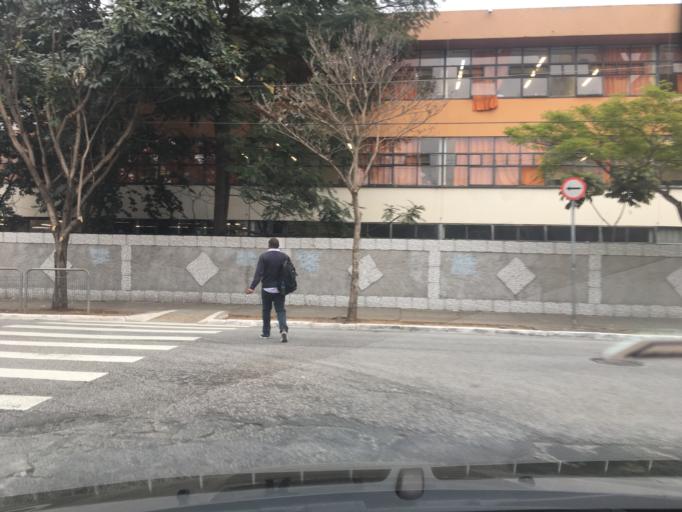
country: BR
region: Sao Paulo
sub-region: Sao Paulo
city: Sao Paulo
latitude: -23.5382
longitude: -46.5791
